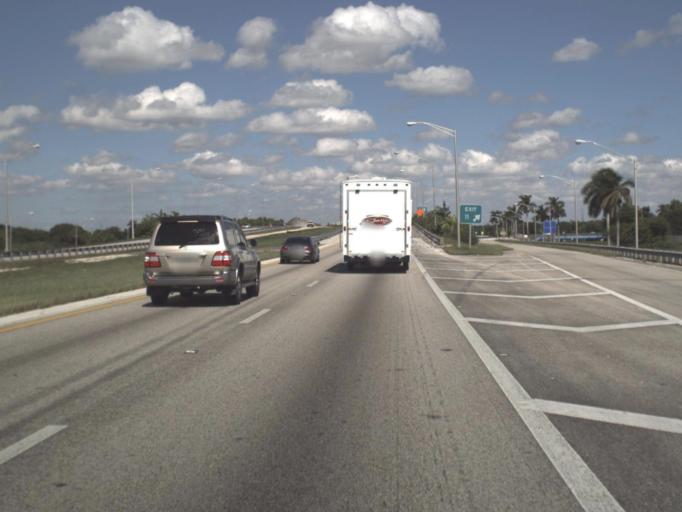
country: US
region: Florida
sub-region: Miami-Dade County
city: Goulds
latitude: 25.5627
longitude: -80.3627
